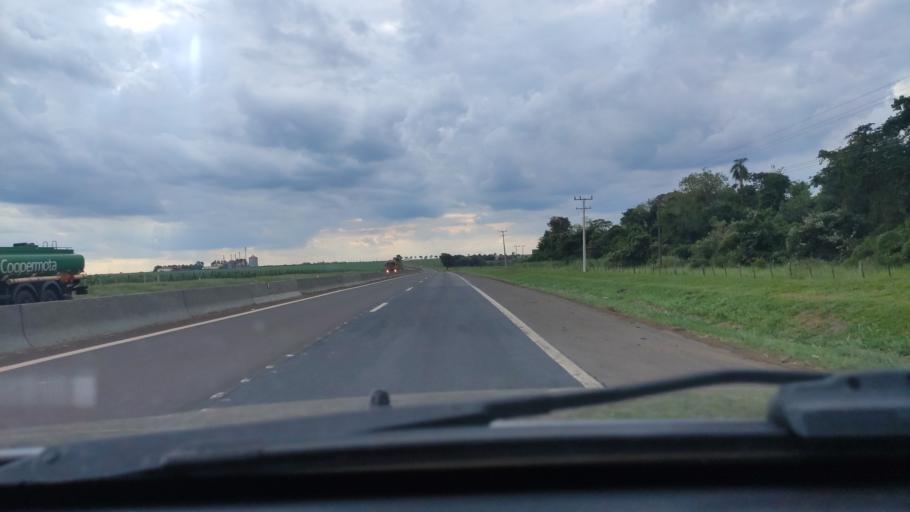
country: BR
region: Sao Paulo
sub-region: Palmital
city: Palmital
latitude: -22.8316
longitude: -50.0263
